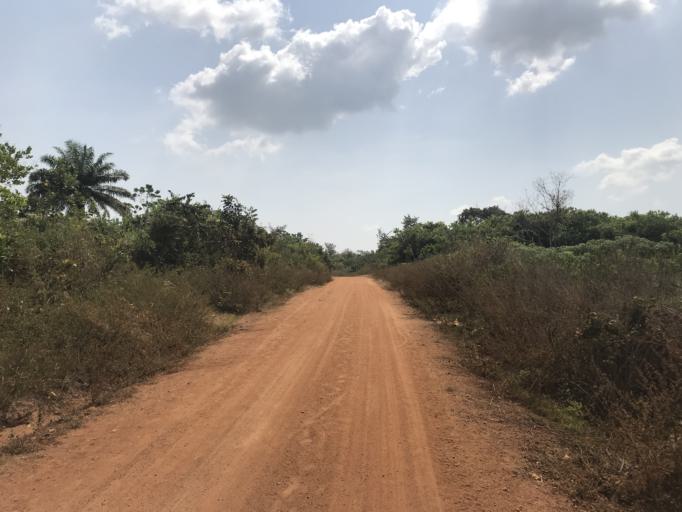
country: NG
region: Osun
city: Ifon
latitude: 7.9896
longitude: 4.5161
